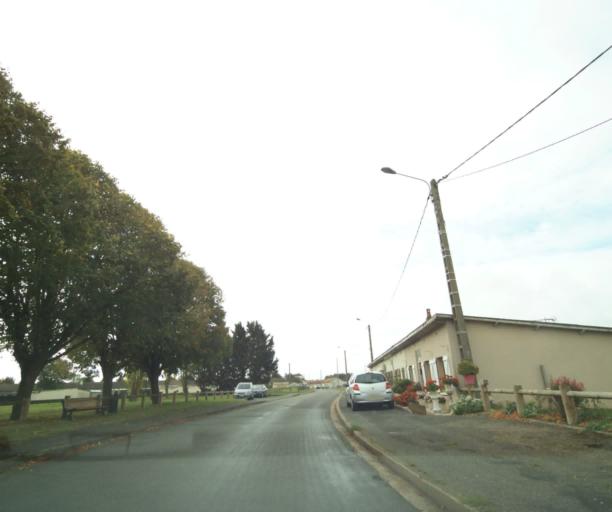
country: FR
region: Centre
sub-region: Departement d'Eure-et-Loir
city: Dreux
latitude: 48.7485
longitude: 1.3411
